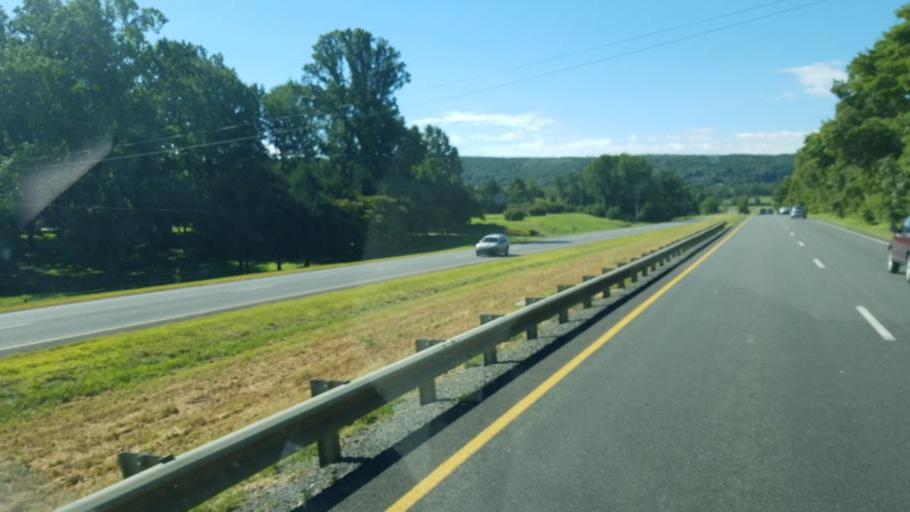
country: US
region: Virginia
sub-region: Fauquier County
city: Marshall
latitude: 38.8120
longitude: -77.8133
